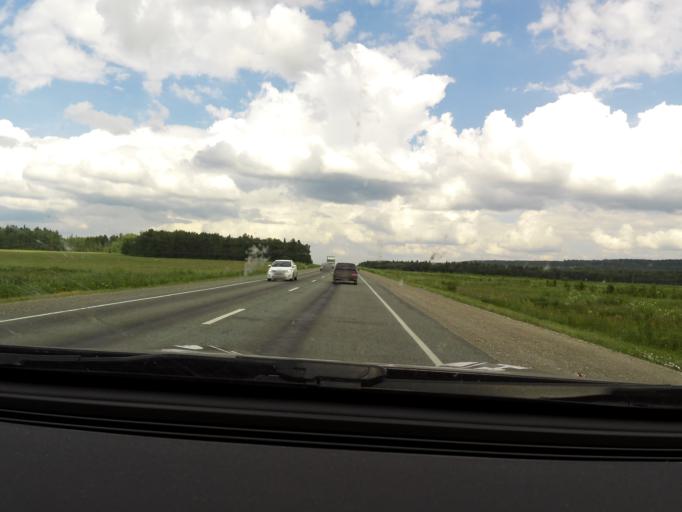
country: RU
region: Sverdlovsk
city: Bisert'
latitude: 56.8109
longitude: 58.7349
